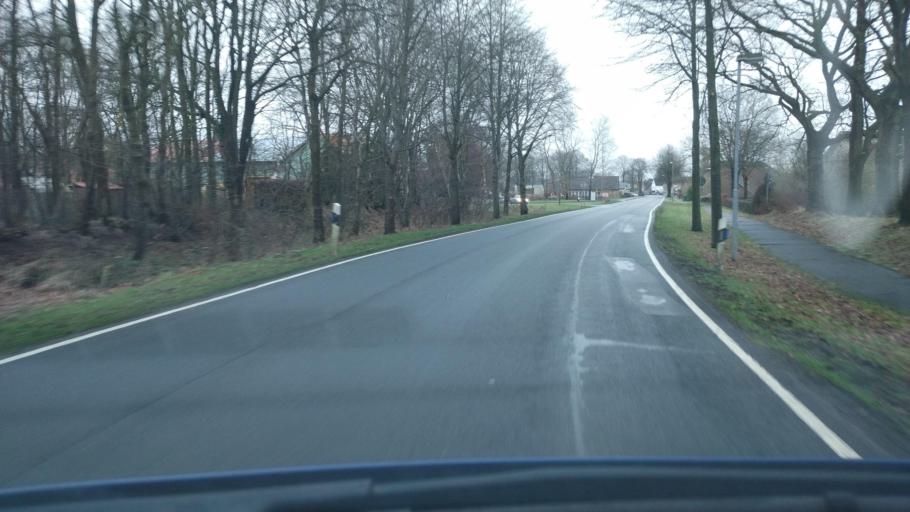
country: DE
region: Schleswig-Holstein
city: Gross Rheide
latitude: 54.4443
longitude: 9.4291
